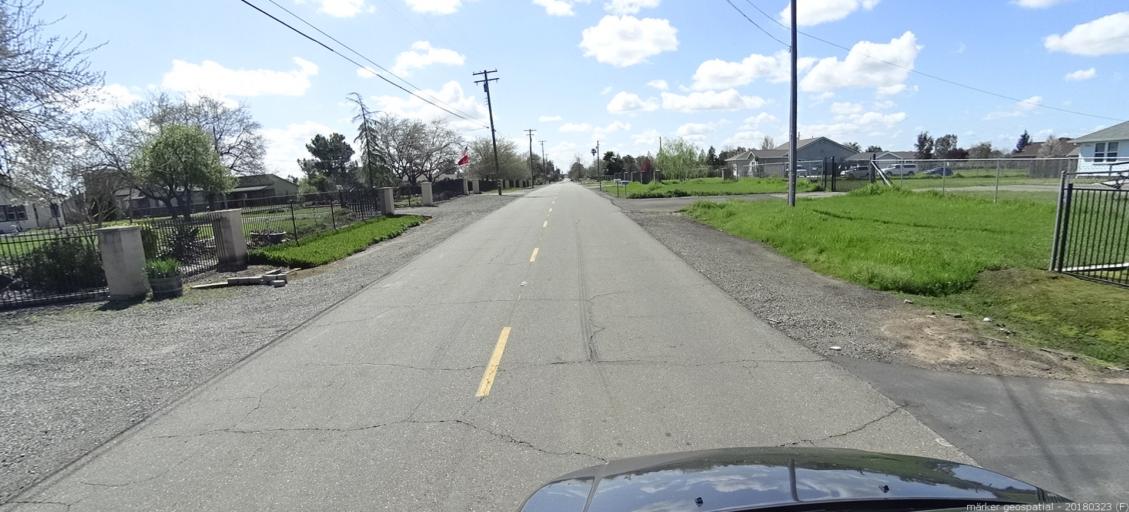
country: US
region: California
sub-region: Sacramento County
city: North Highlands
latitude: 38.6821
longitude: -121.4107
